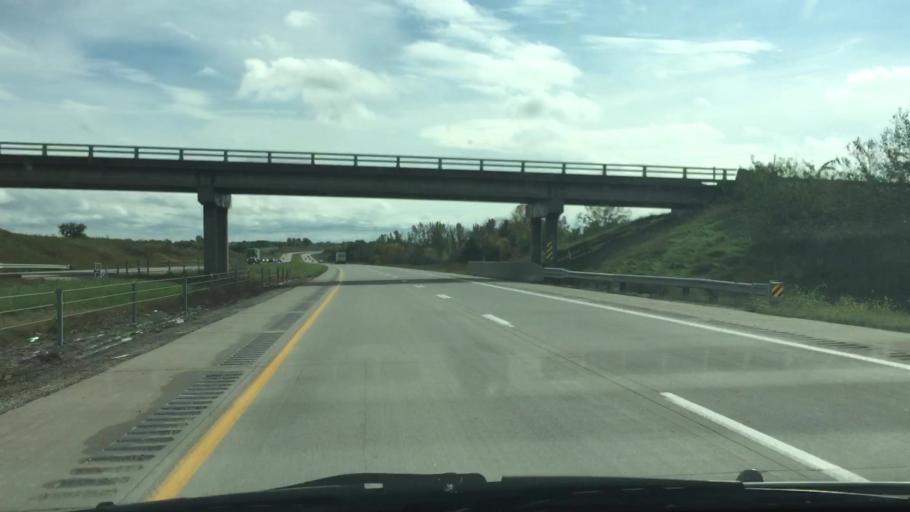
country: US
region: Iowa
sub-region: Clarke County
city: Osceola
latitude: 40.9139
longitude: -93.7976
